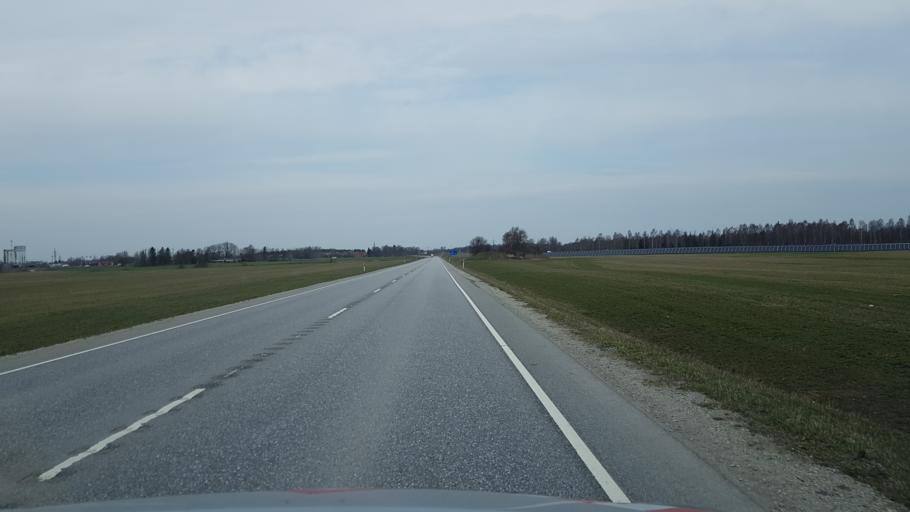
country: EE
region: Laeaene-Virumaa
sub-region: Someru vald
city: Someru
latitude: 59.3504
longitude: 26.4021
